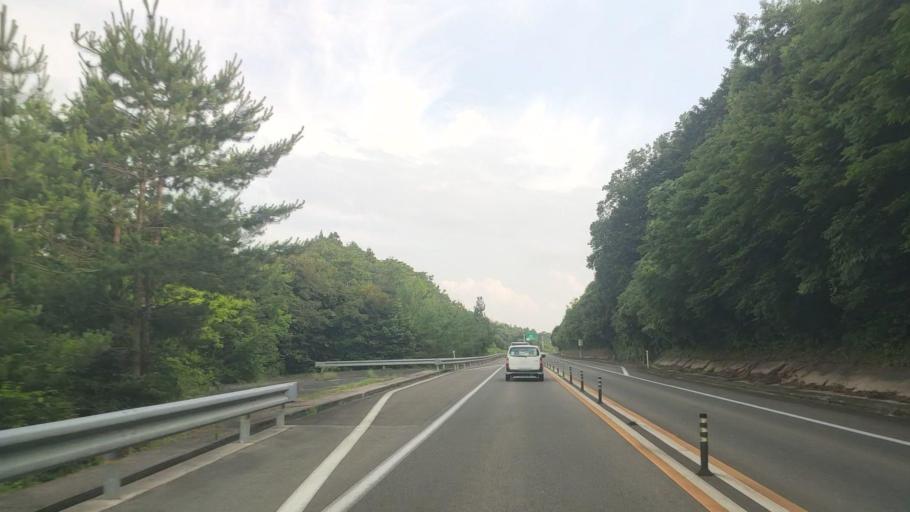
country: JP
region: Tottori
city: Kurayoshi
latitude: 35.4582
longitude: 133.8102
